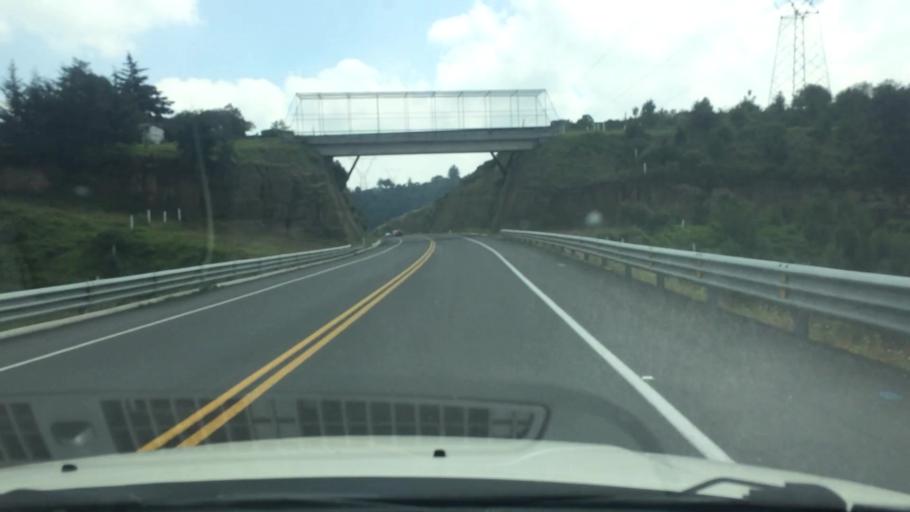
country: MX
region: Mexico
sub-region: Almoloya de Juarez
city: San Pedro de la Hortaliza (Ejido Almoloyan)
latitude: 19.3764
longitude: -99.8731
